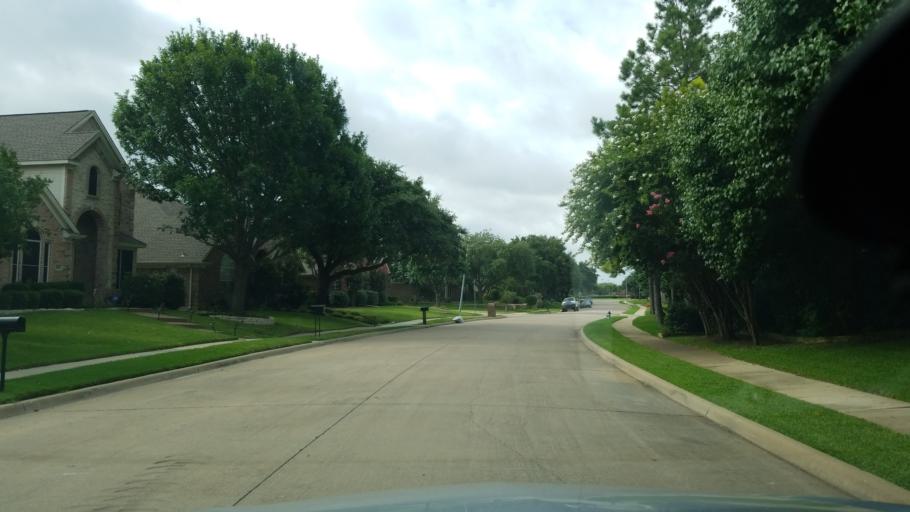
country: US
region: Texas
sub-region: Dallas County
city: Farmers Branch
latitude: 32.9457
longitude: -96.9505
